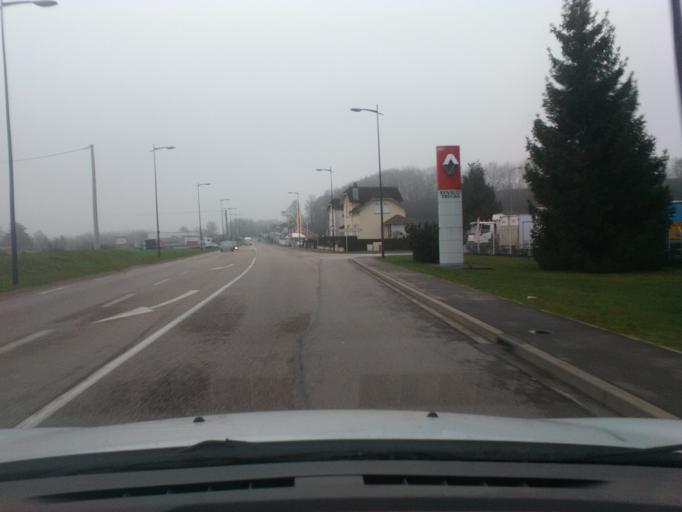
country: FR
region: Lorraine
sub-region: Departement des Vosges
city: Golbey
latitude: 48.2140
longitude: 6.4393
